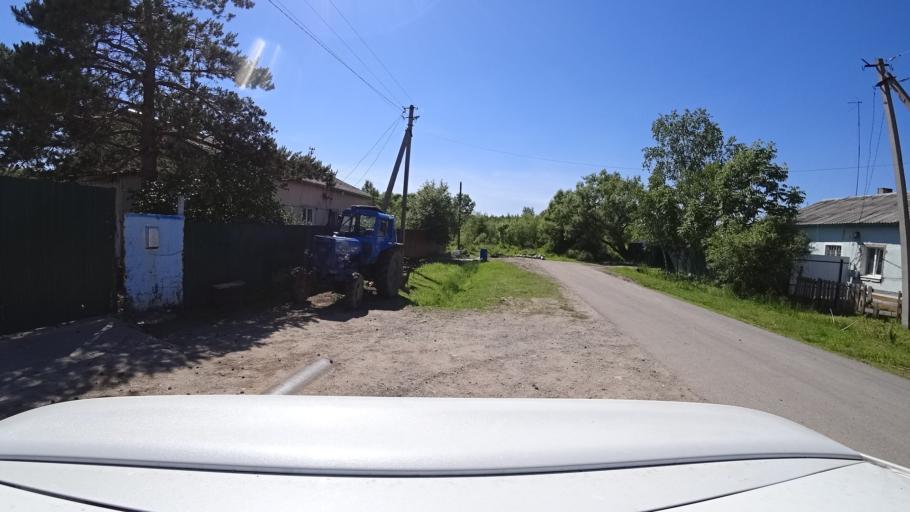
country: RU
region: Khabarovsk Krai
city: Topolevo
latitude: 48.5571
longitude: 135.1868
